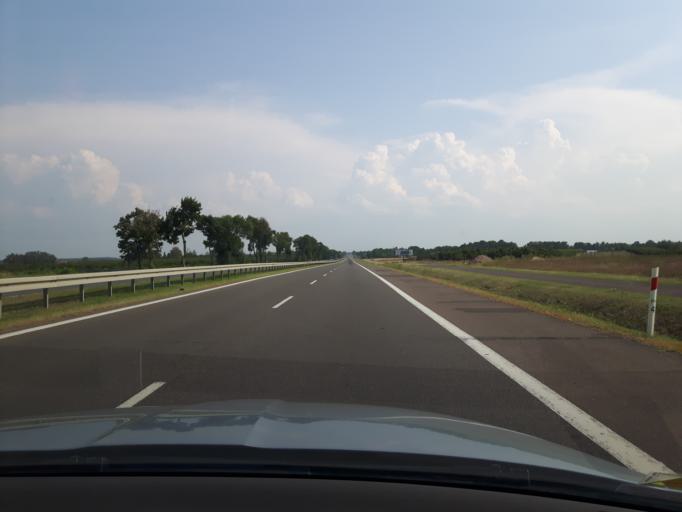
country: PL
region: Masovian Voivodeship
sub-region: Powiat plonski
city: Zaluski
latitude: 52.5745
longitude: 20.4822
